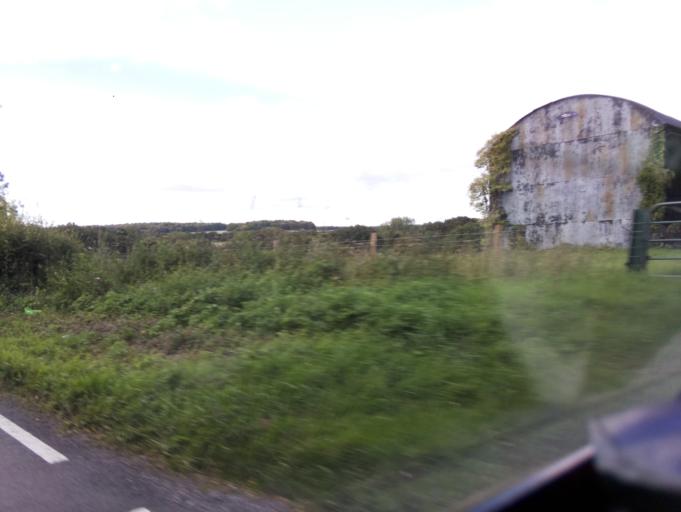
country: GB
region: England
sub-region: Hampshire
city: Winchester
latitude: 51.0996
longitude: -1.3971
